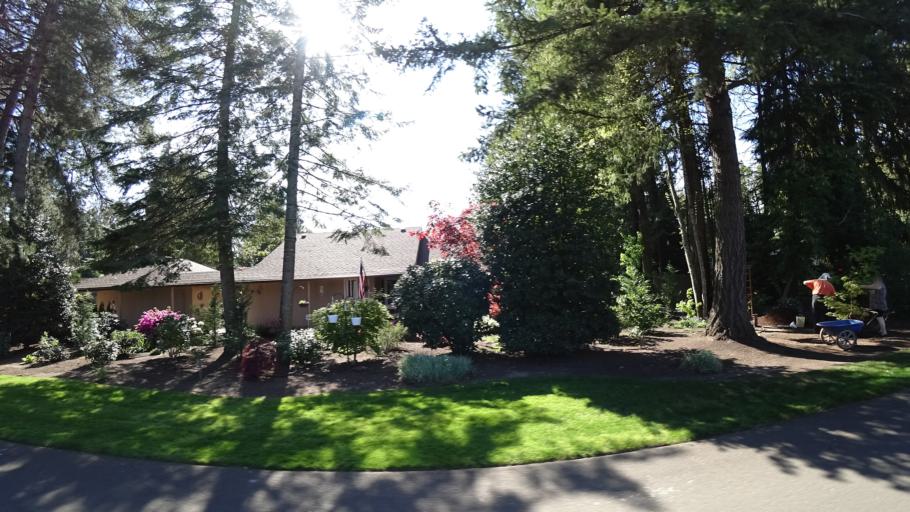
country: US
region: Oregon
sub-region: Washington County
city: Hillsboro
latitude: 45.5311
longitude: -122.9859
